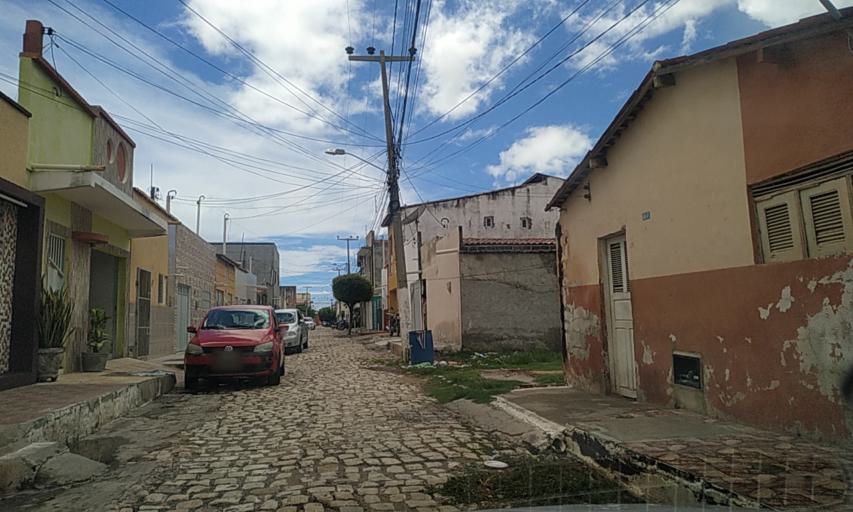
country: BR
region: Rio Grande do Norte
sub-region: Areia Branca
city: Areia Branca
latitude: -4.9596
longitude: -37.1354
